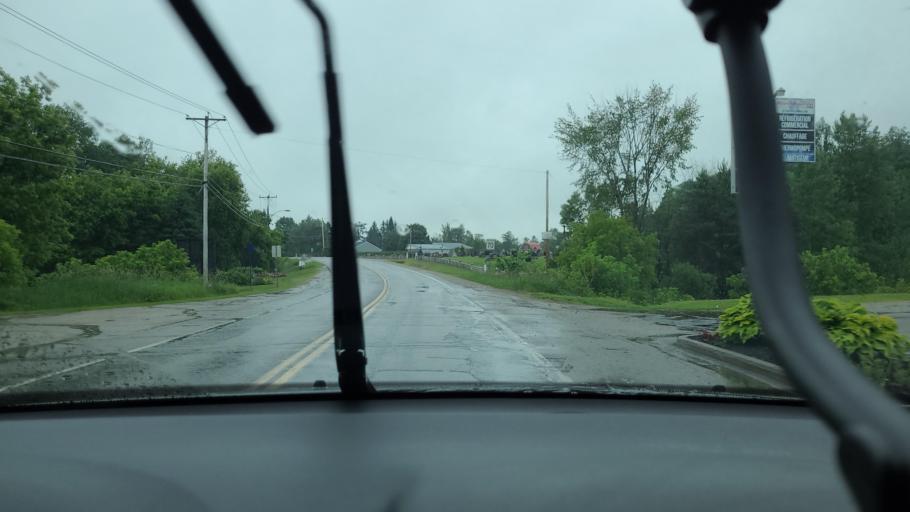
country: CA
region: Quebec
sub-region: Outaouais
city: Saint-Andre-Avellin
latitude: 45.7172
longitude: -75.0575
